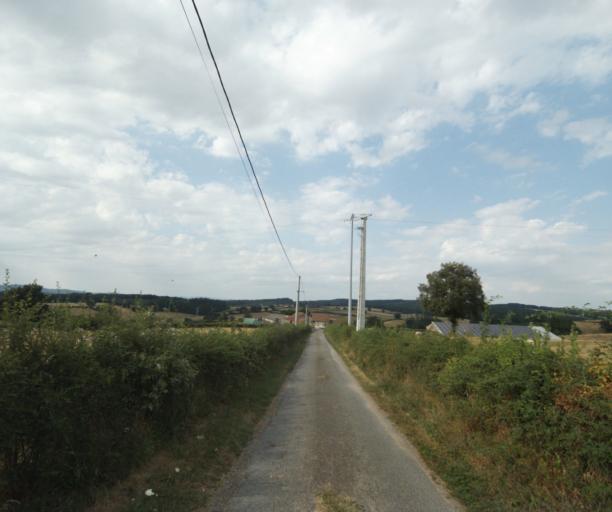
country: FR
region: Bourgogne
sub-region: Departement de Saone-et-Loire
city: Gueugnon
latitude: 46.6021
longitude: 4.1009
